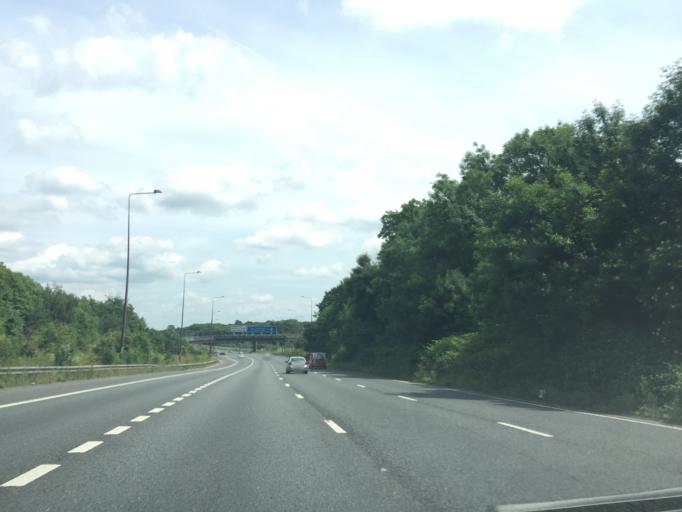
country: GB
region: England
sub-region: Medway
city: Cuxton
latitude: 51.4006
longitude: 0.4296
